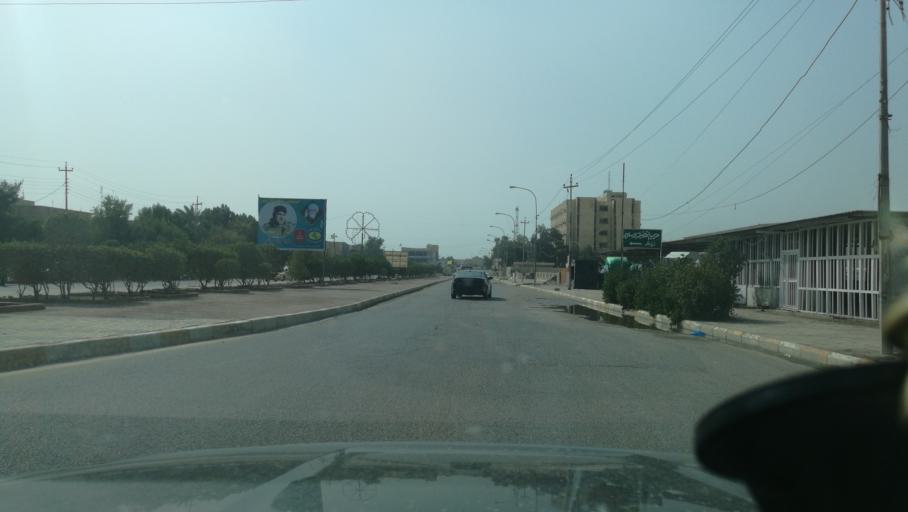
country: IQ
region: Dhi Qar
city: An Nasiriyah
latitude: 31.0551
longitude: 46.2468
